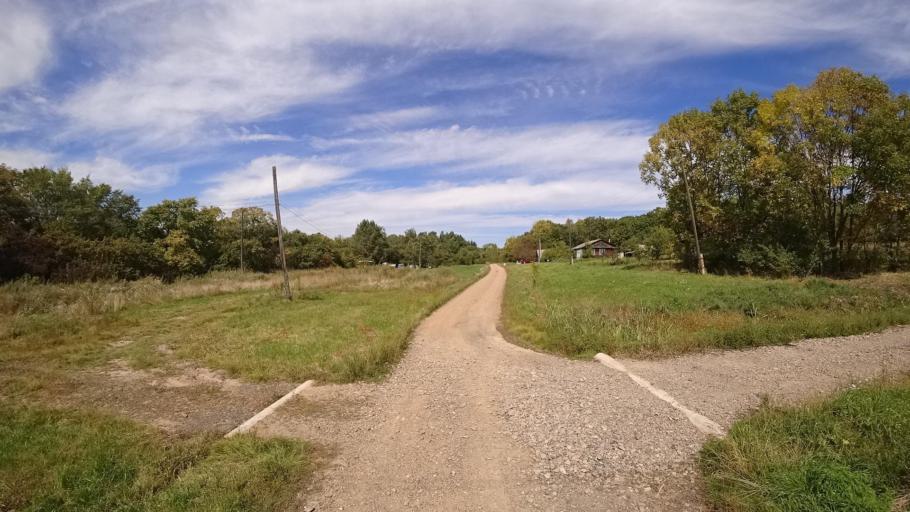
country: RU
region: Primorskiy
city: Yakovlevka
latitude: 44.6478
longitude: 133.5879
